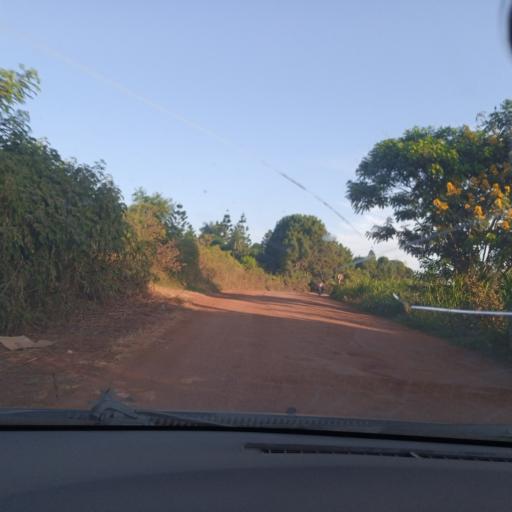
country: UG
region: Central Region
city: Masaka
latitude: -0.3381
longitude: 31.7626
